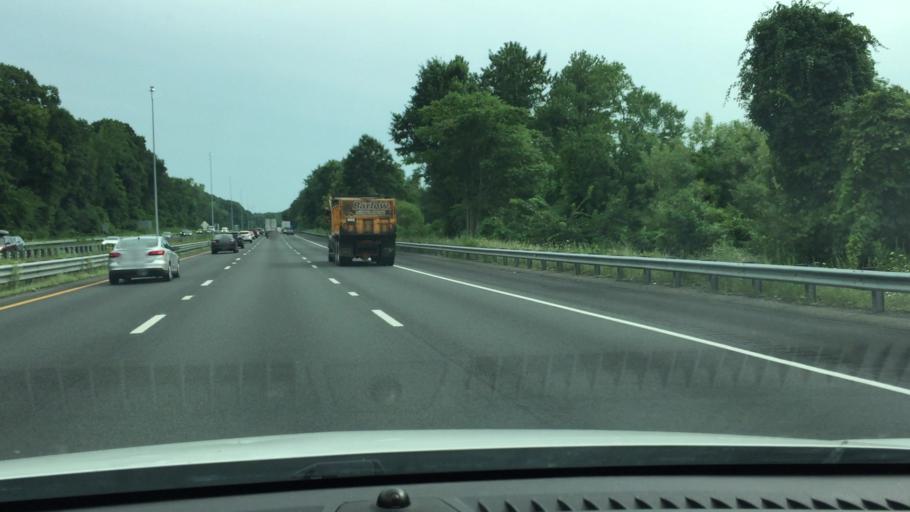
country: US
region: Massachusetts
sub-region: Hampden County
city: Longmeadow
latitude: 42.0487
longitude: -72.5892
